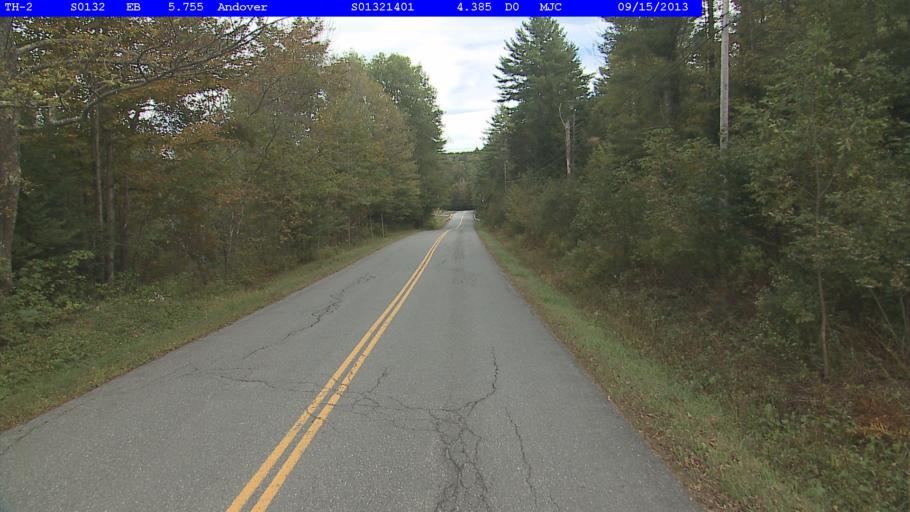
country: US
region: Vermont
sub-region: Windsor County
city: Chester
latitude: 43.2747
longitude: -72.6913
